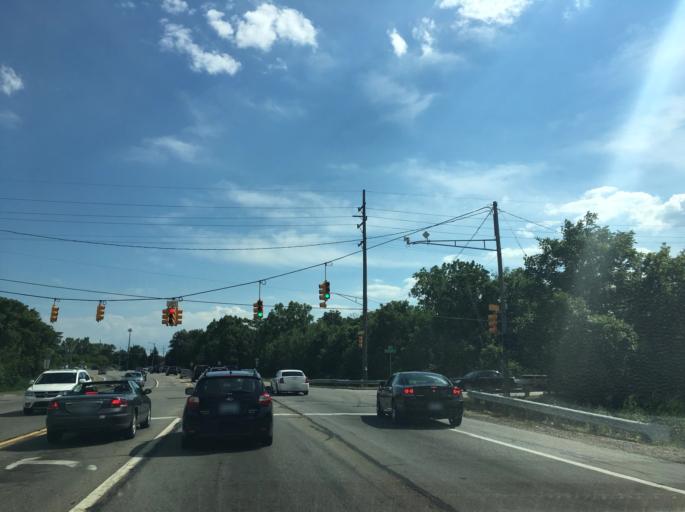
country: US
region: Michigan
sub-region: Macomb County
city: Clinton
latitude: 42.5882
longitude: -82.9031
